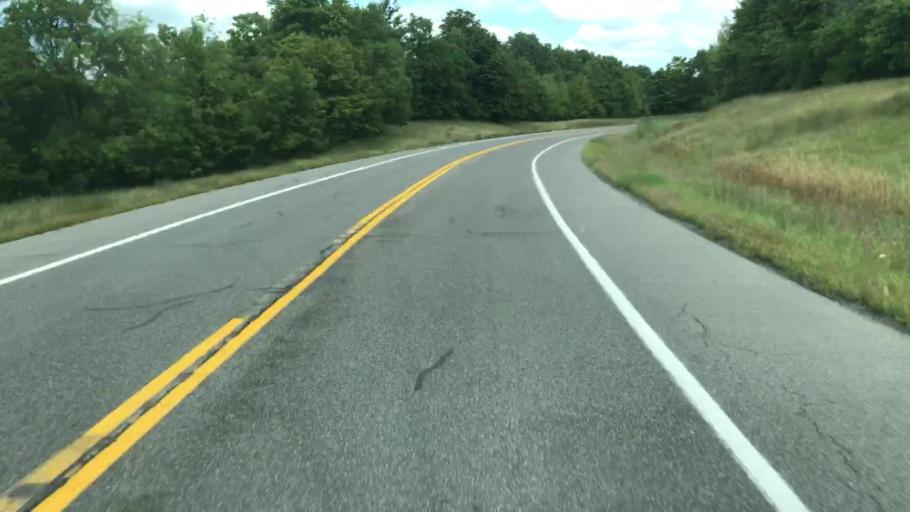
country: US
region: New York
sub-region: Onondaga County
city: Marcellus
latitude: 42.9529
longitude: -76.3707
